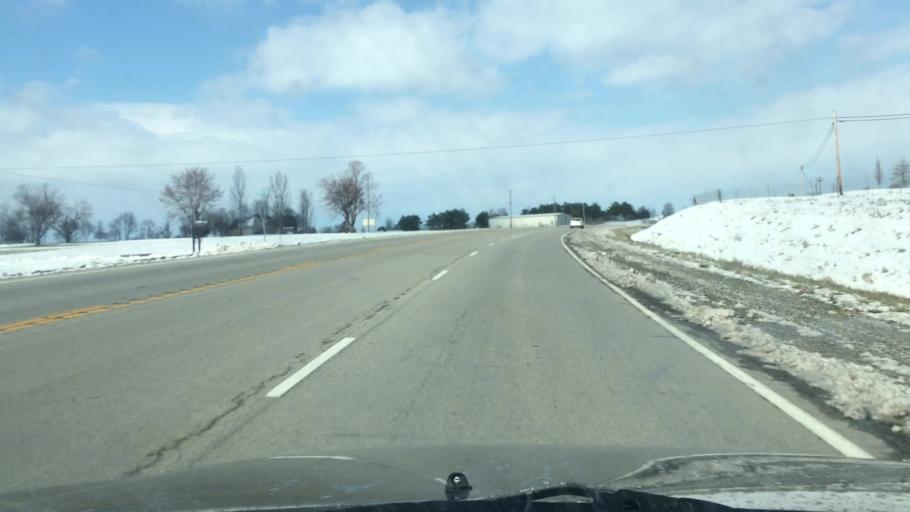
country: US
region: Kentucky
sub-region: Marion County
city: Lebanon
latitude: 37.5451
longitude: -85.3035
